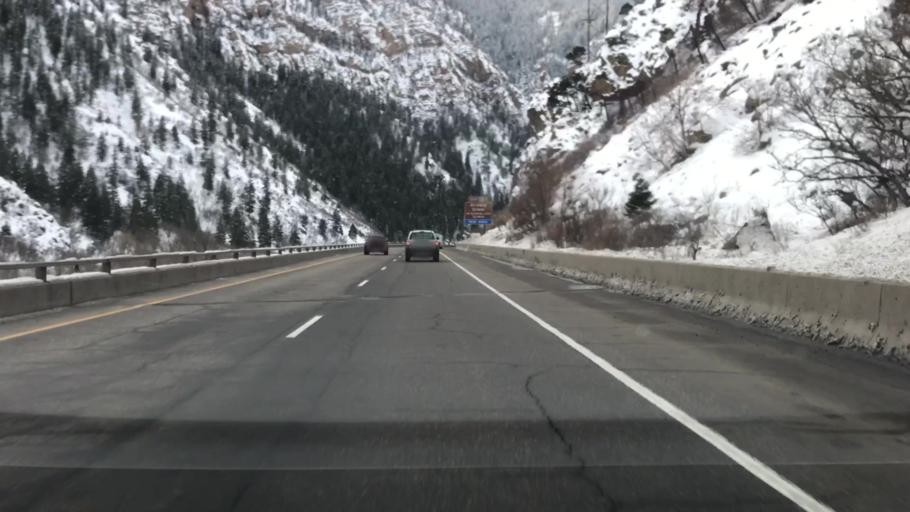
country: US
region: Colorado
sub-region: Garfield County
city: Glenwood Springs
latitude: 39.5620
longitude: -107.2390
